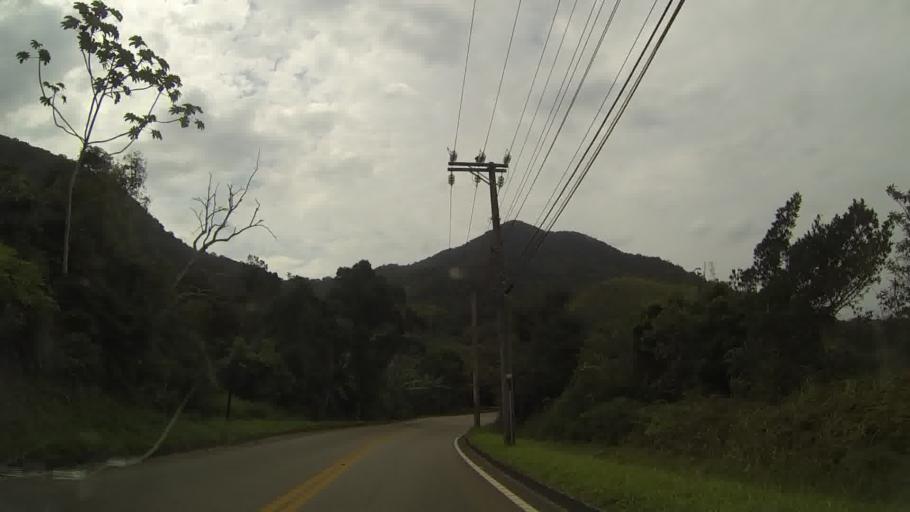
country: BR
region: Sao Paulo
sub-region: Sao Sebastiao
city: Sao Sebastiao
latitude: -23.8266
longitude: -45.5197
